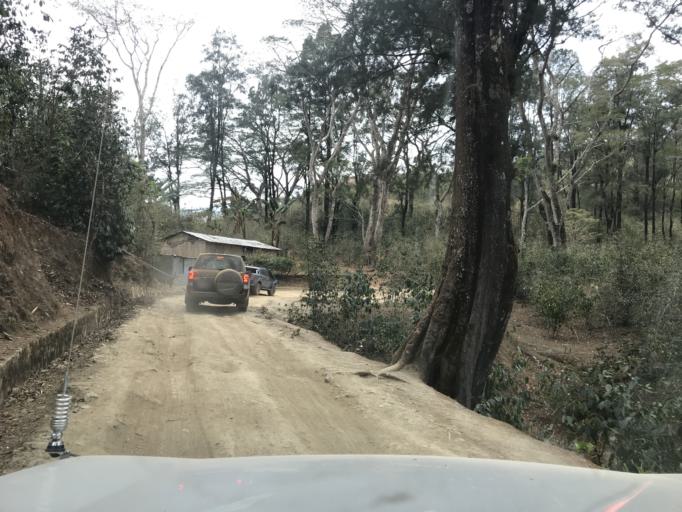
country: TL
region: Ermera
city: Gleno
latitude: -8.8348
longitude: 125.4496
